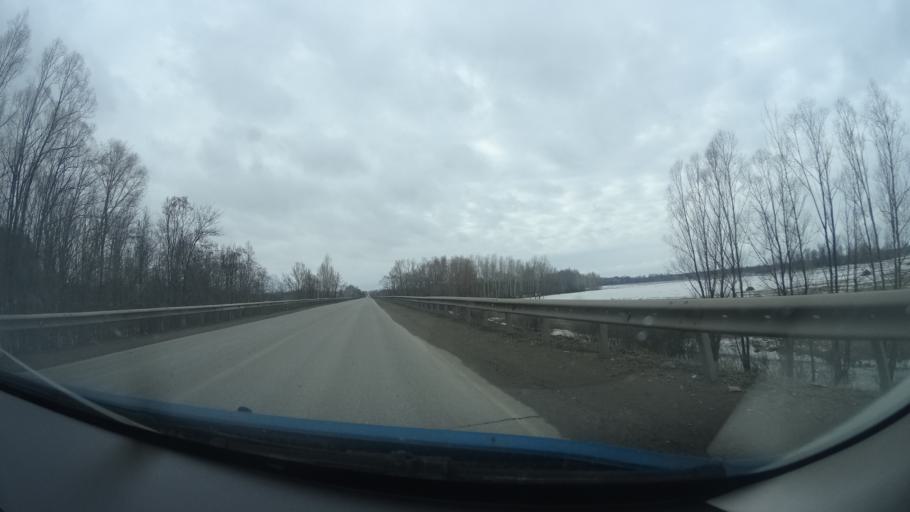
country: RU
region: Bashkortostan
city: Birsk
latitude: 55.4817
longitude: 55.5980
